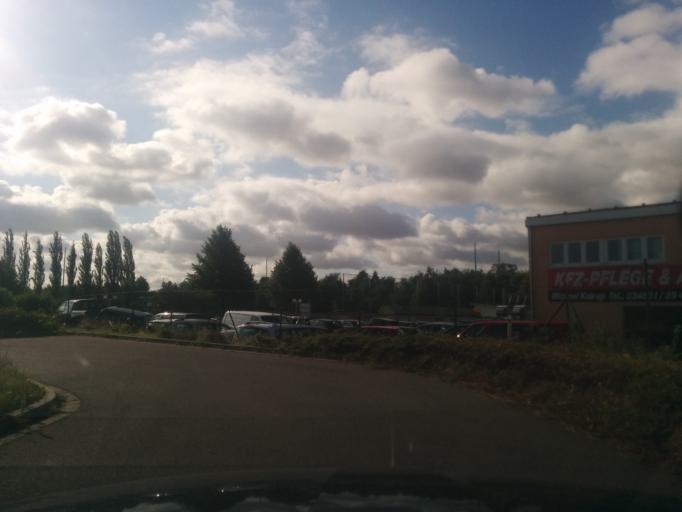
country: DE
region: Saxony-Anhalt
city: Bennstedt
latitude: 51.4670
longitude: 11.8202
